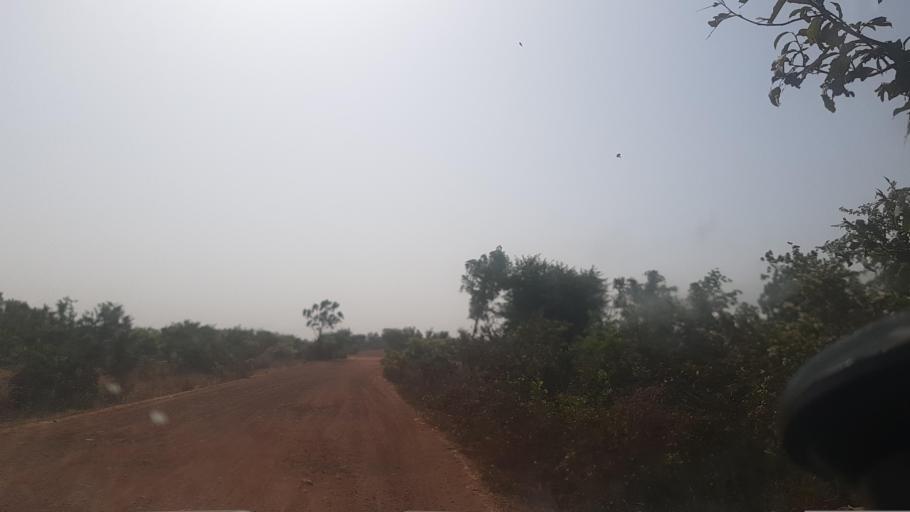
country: ML
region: Segou
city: Baroueli
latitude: 13.1429
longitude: -6.5147
